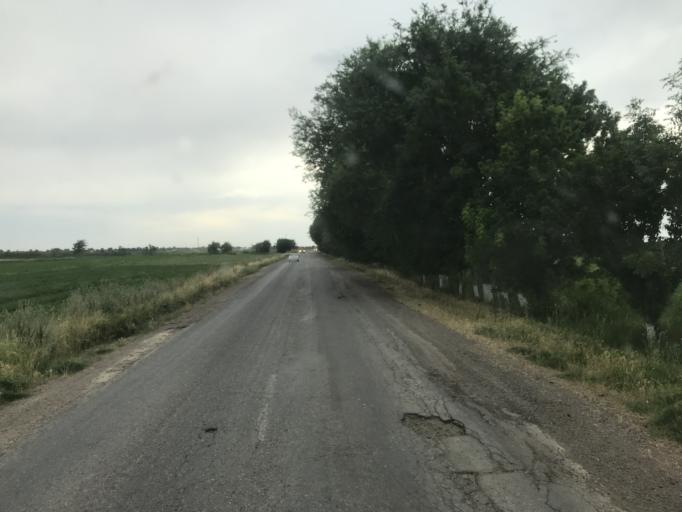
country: KZ
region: Ongtustik Qazaqstan
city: Asykata
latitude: 40.9513
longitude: 68.4478
